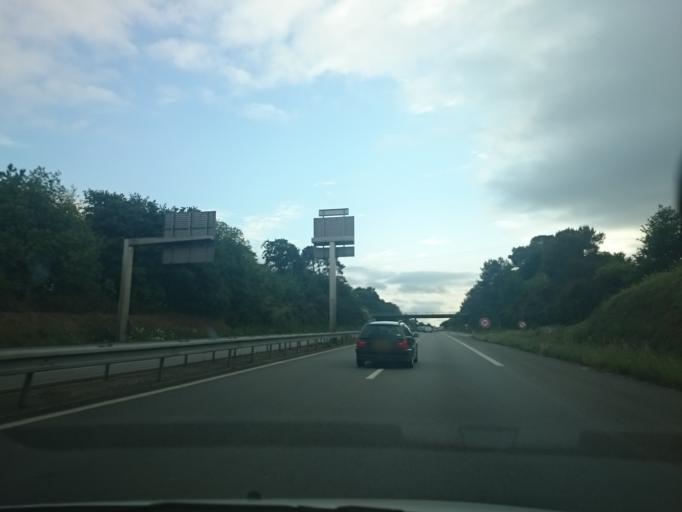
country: FR
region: Brittany
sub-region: Departement du Morbihan
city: Pluneret
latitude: 47.6668
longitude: -2.9551
